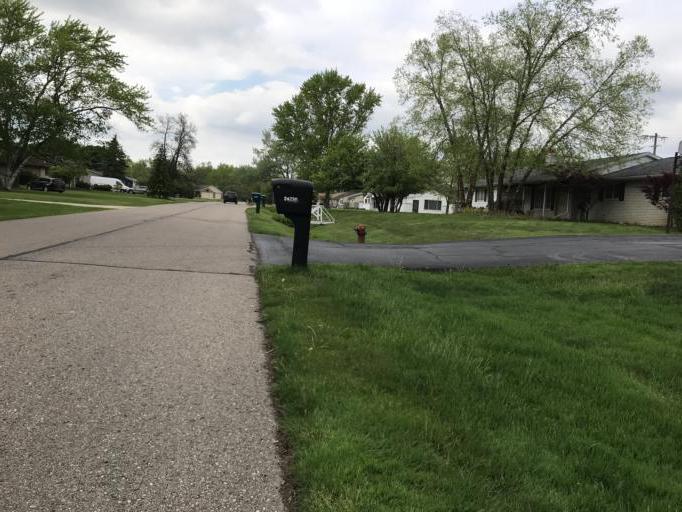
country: US
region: Michigan
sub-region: Oakland County
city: Farmington
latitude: 42.4752
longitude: -83.3434
